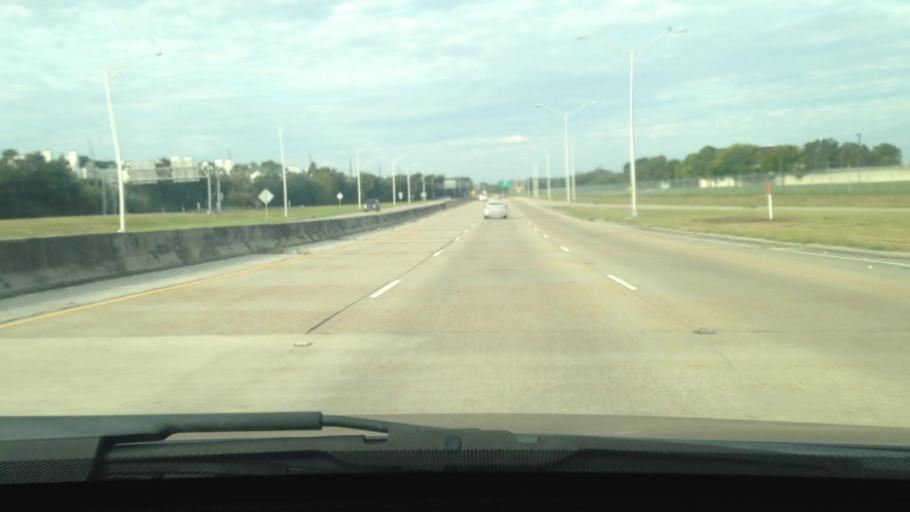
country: US
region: Louisiana
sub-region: Jefferson Parish
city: Elmwood
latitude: 29.9685
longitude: -90.1856
